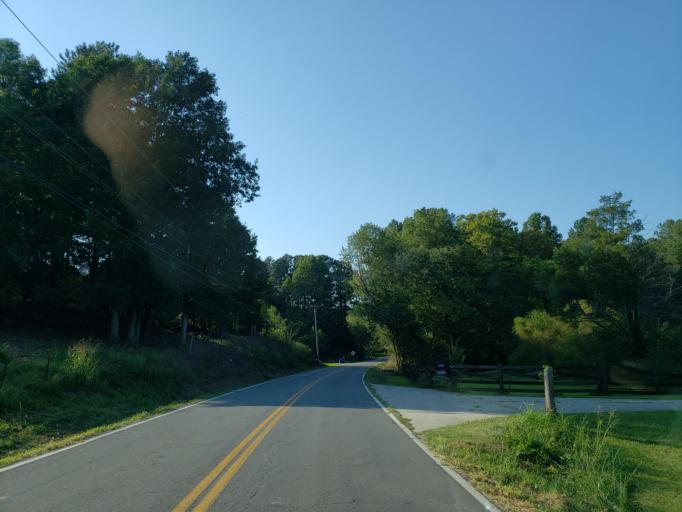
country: US
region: Tennessee
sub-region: Bradley County
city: Wildwood Lake
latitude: 35.0575
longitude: -84.7628
